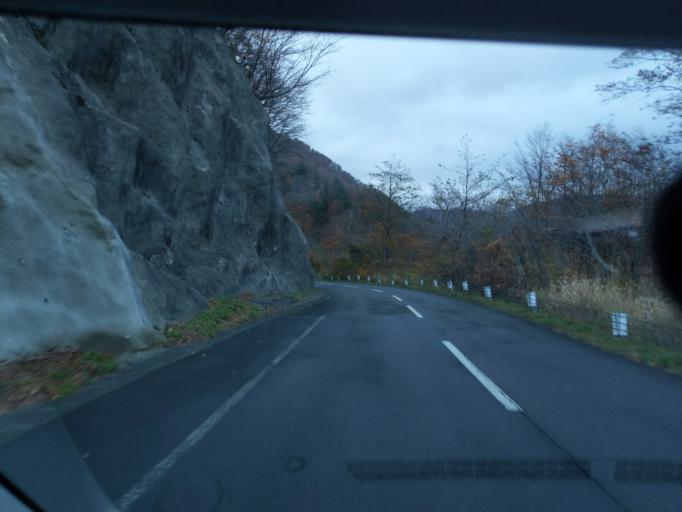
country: JP
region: Iwate
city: Mizusawa
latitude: 39.1223
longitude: 140.8295
